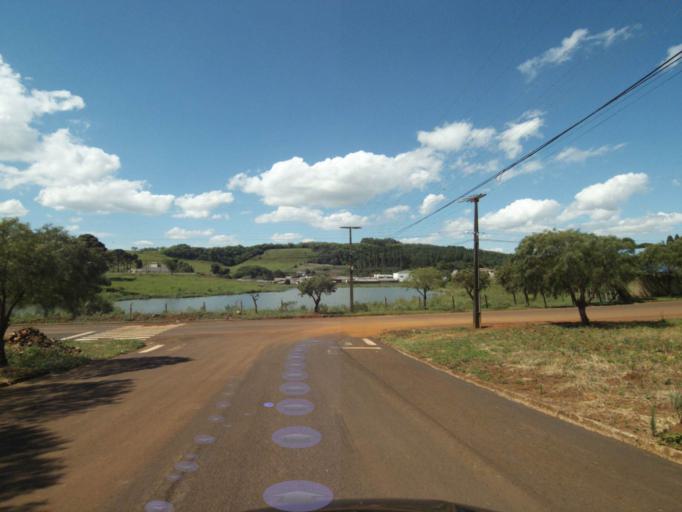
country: BR
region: Parana
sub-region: Coronel Vivida
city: Coronel Vivida
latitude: -26.1459
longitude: -52.3821
